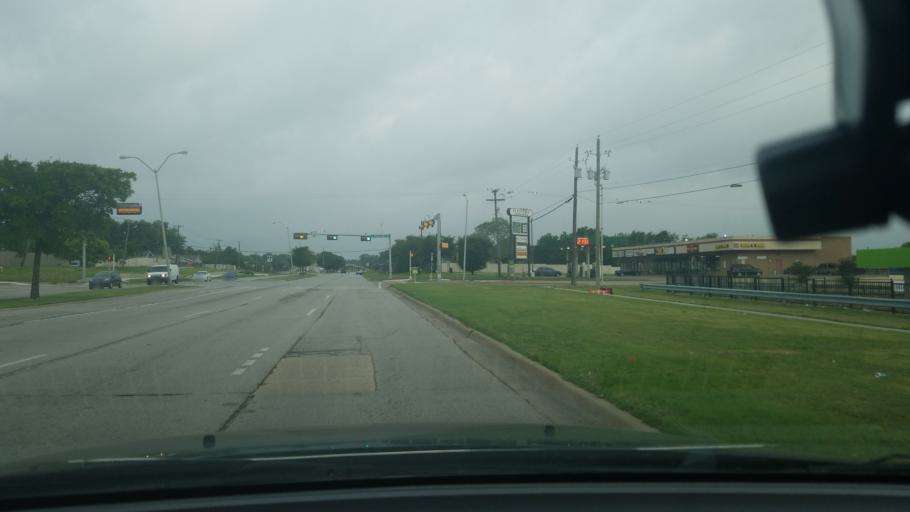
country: US
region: Texas
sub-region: Dallas County
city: Mesquite
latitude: 32.7681
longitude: -96.6291
